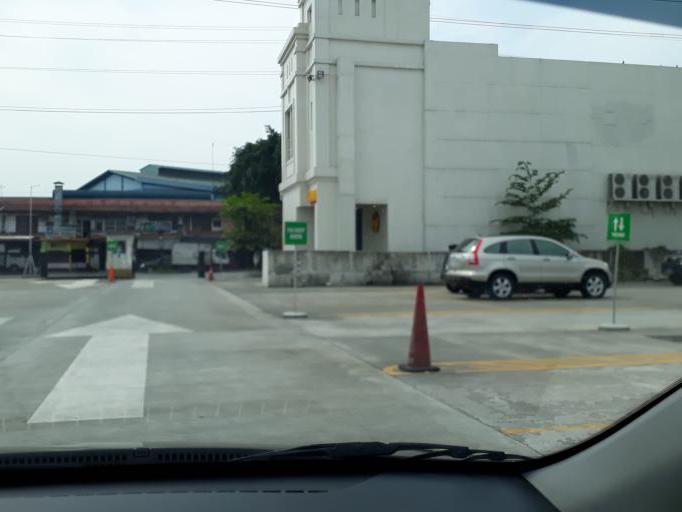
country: PH
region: Metro Manila
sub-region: City of Manila
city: Quiapo
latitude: 14.5908
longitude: 120.9991
